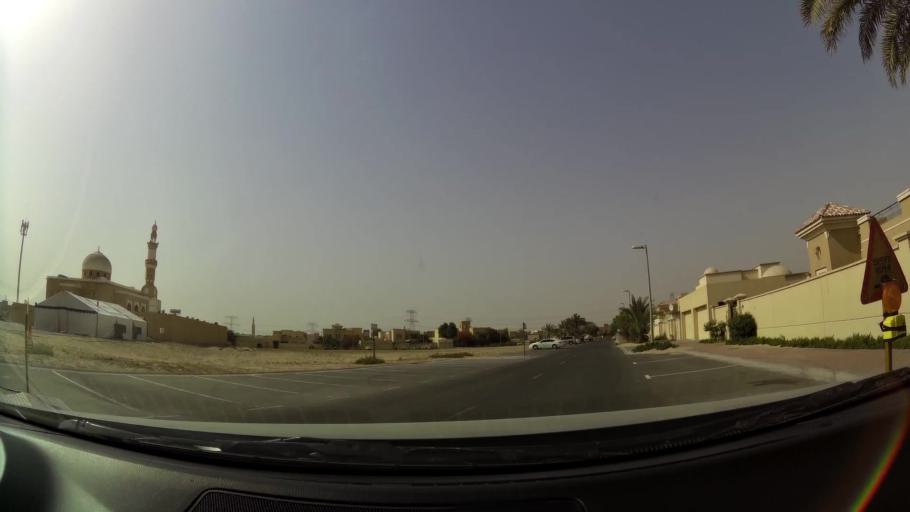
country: AE
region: Ash Shariqah
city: Sharjah
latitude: 25.2691
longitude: 55.4563
